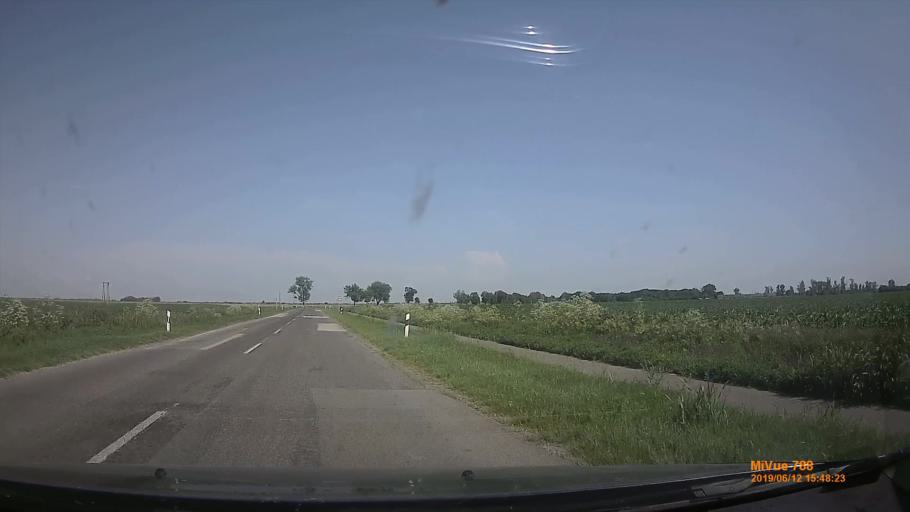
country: HU
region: Csongrad
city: Apatfalva
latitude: 46.2025
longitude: 20.5482
